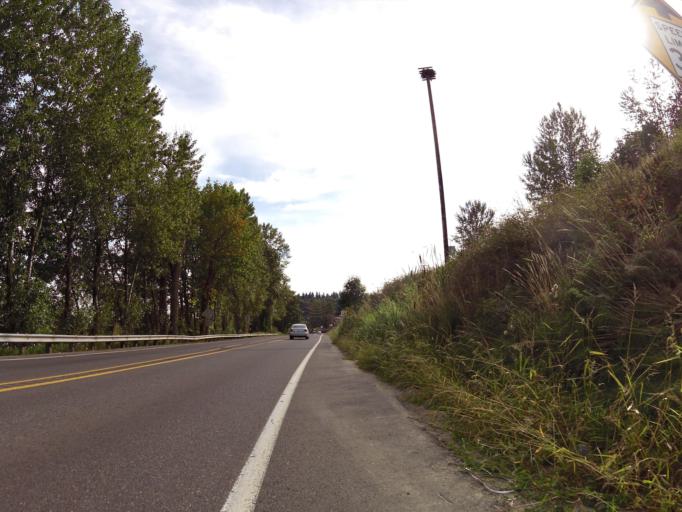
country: US
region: Washington
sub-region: Cowlitz County
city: West Side Highway
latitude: 46.1683
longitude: -122.9153
